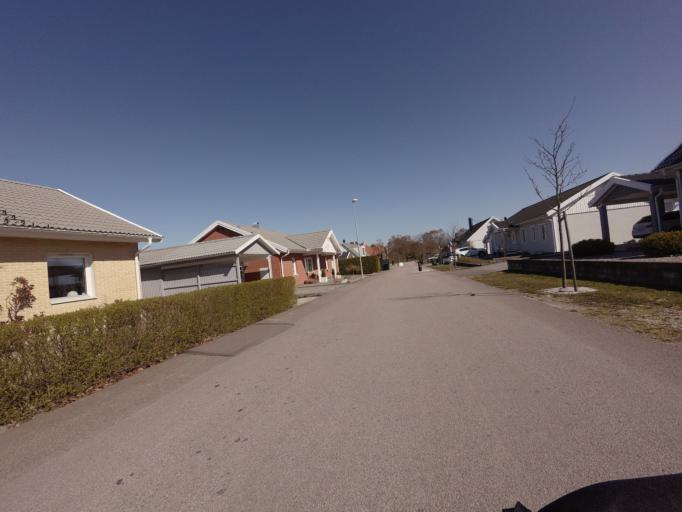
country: SE
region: Skane
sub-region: Malmo
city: Oxie
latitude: 55.4635
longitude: 13.1398
